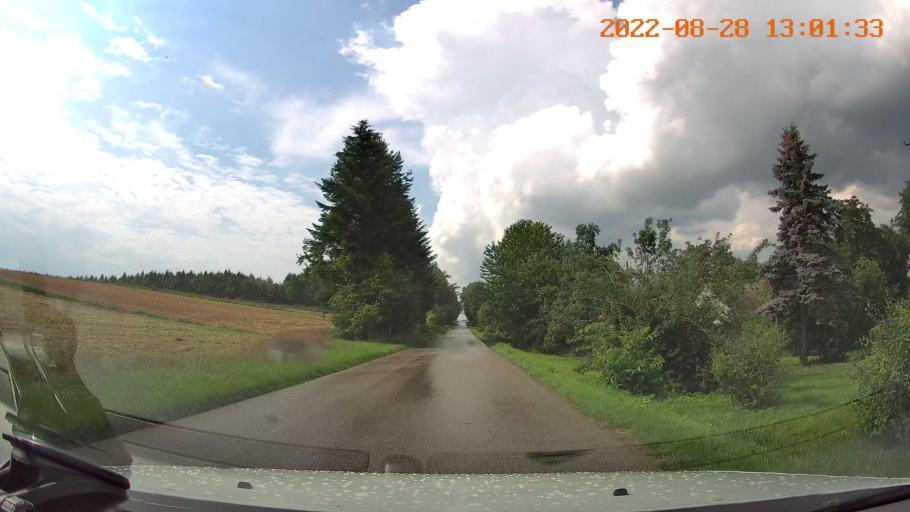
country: PL
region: Lesser Poland Voivodeship
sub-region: Powiat miechowski
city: Miechow
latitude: 50.3570
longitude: 20.1398
